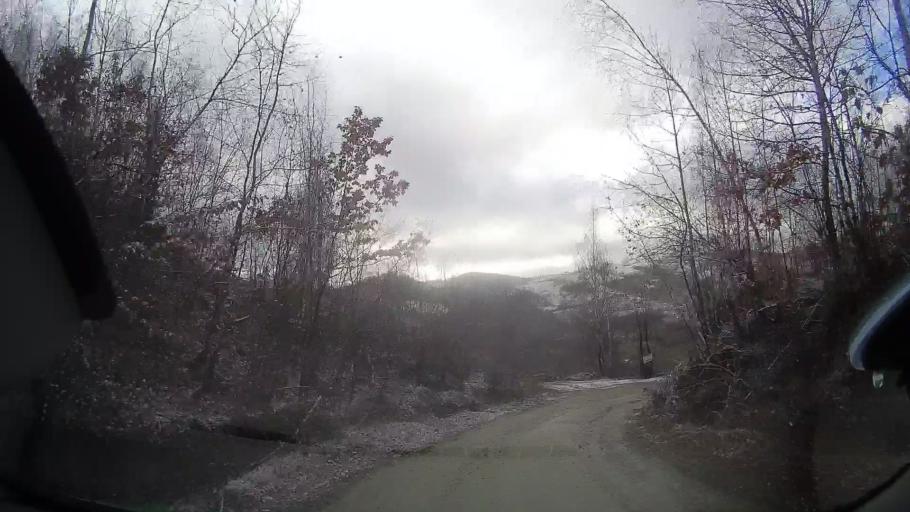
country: RO
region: Cluj
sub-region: Comuna Valea Ierii
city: Valea Ierii
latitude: 46.6728
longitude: 23.3180
